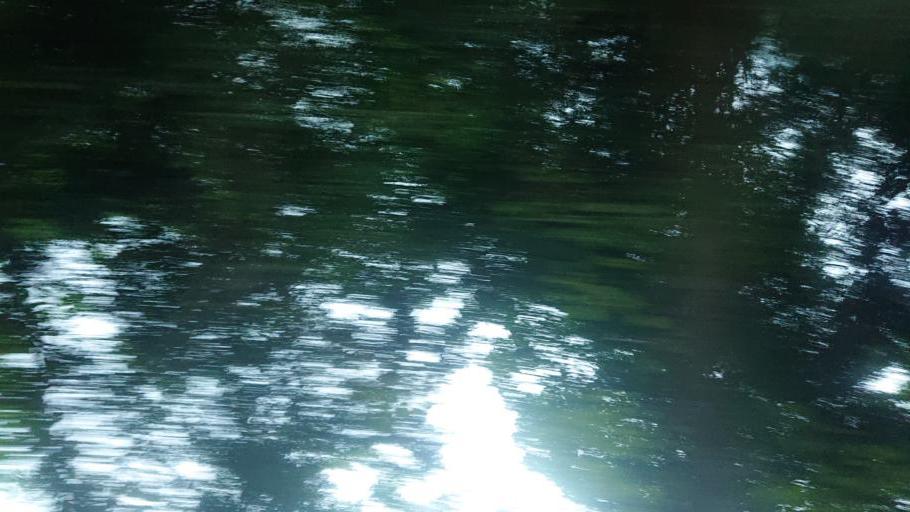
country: TW
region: Taiwan
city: Lugu
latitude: 23.5887
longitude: 120.7240
